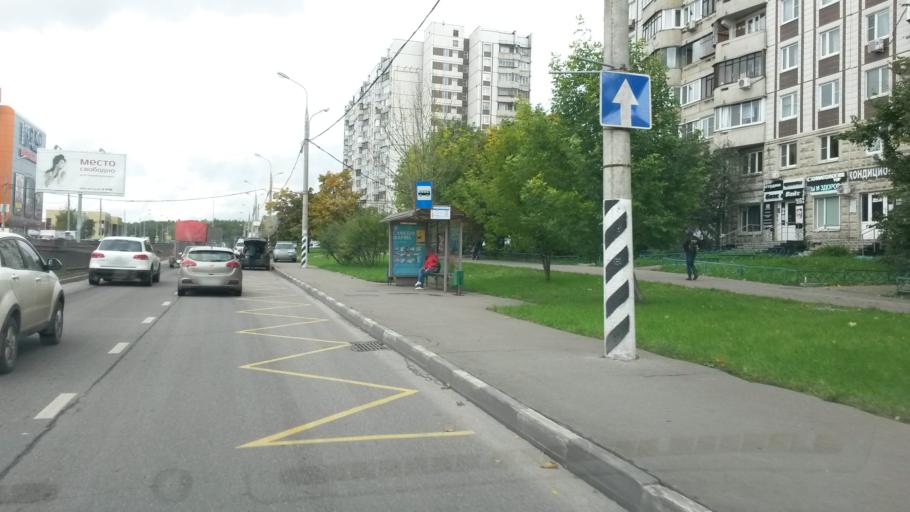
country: RU
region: Moskovskaya
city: Shcherbinka
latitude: 55.5471
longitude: 37.5454
